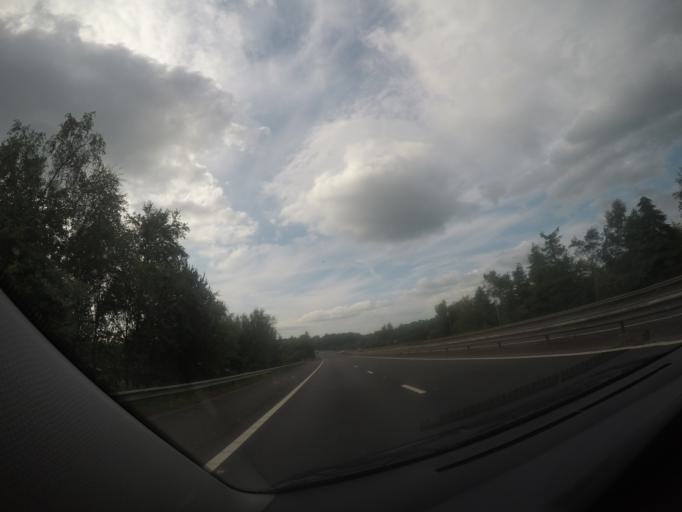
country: GB
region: Scotland
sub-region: South Lanarkshire
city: Douglas
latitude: 55.5750
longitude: -3.8134
